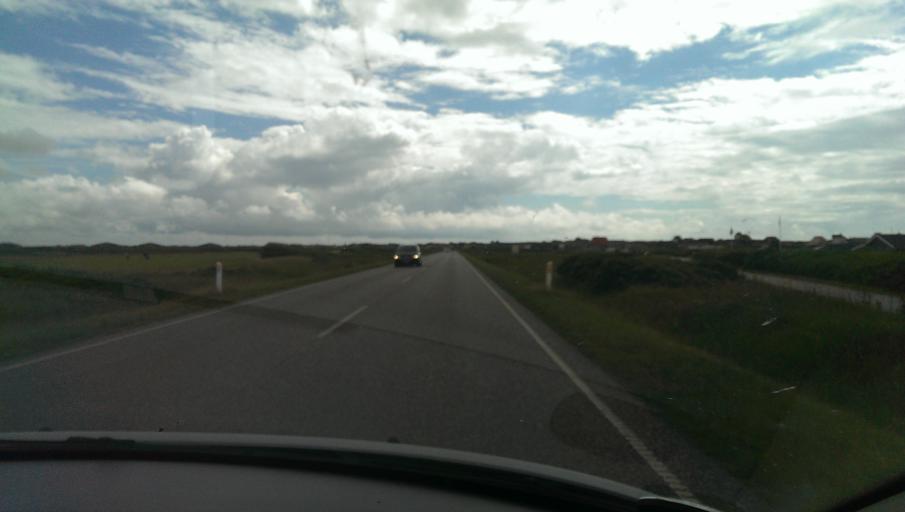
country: DK
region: Central Jutland
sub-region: Ringkobing-Skjern Kommune
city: Hvide Sande
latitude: 56.1301
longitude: 8.1195
